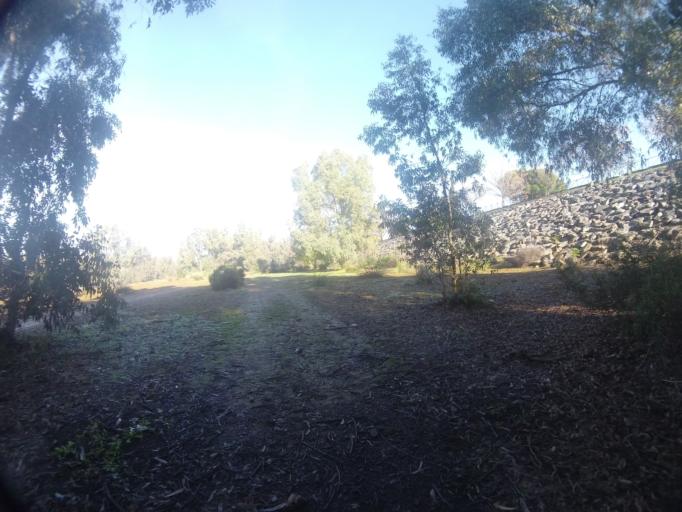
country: ES
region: Andalusia
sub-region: Provincia de Huelva
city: Gibraleon
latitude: 37.3739
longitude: -6.9757
